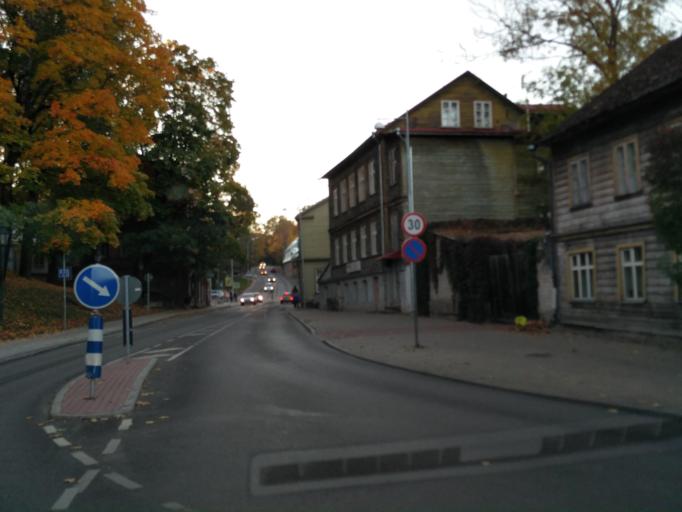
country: EE
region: Tartu
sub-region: Tartu linn
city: Tartu
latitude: 58.3821
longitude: 26.7165
